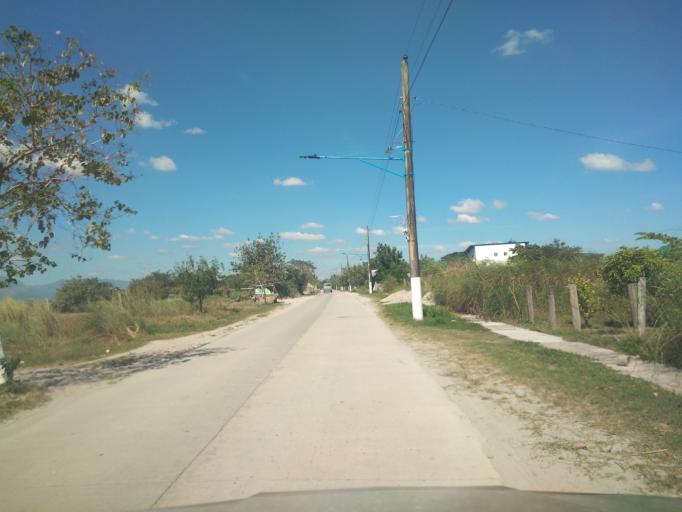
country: PH
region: Central Luzon
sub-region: Province of Pampanga
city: San Basilio
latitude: 15.0375
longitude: 120.6198
